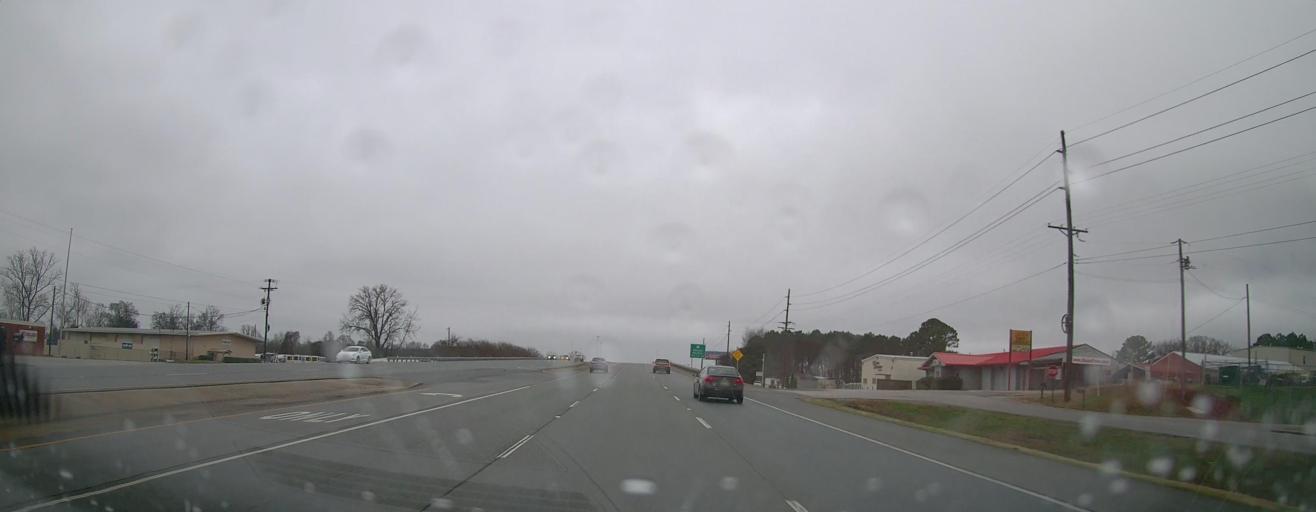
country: US
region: Alabama
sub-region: Morgan County
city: Decatur
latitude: 34.6123
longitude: -87.0312
